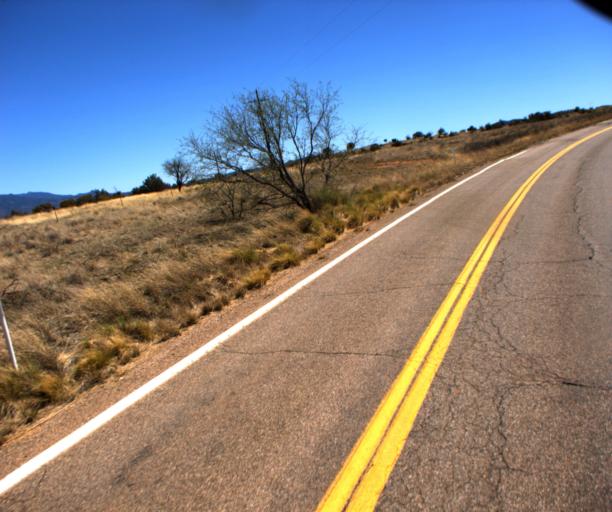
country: US
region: Arizona
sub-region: Cochise County
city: Huachuca City
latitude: 31.5761
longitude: -110.5543
